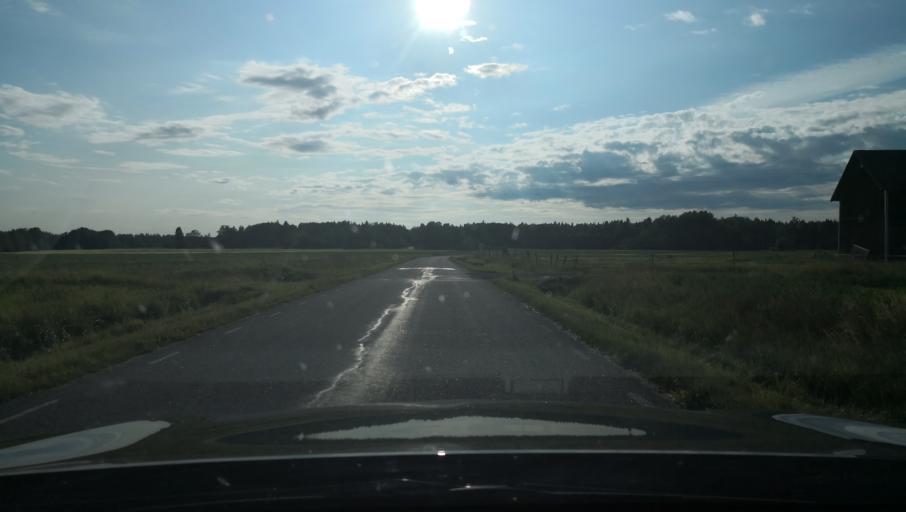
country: SE
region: Uppsala
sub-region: Osthammars Kommun
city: Osterbybruk
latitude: 60.0193
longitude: 17.9706
